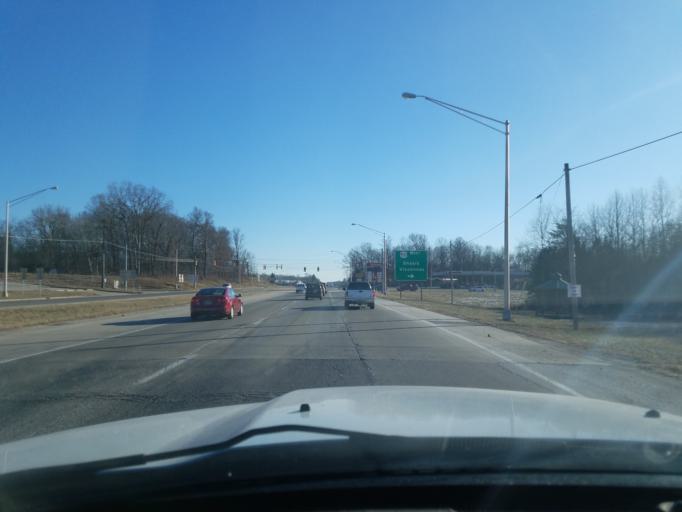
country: US
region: Indiana
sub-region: Lawrence County
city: Bedford
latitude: 38.8137
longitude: -86.5173
